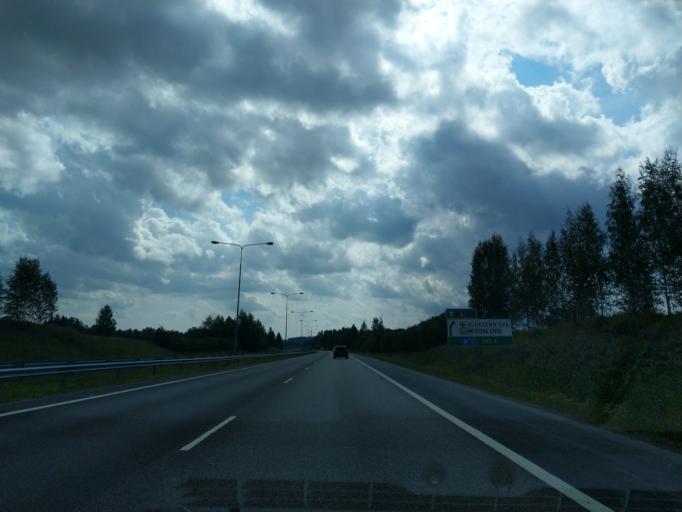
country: FI
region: South Karelia
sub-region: Imatra
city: Ruokolahti
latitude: 61.2298
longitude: 28.8560
